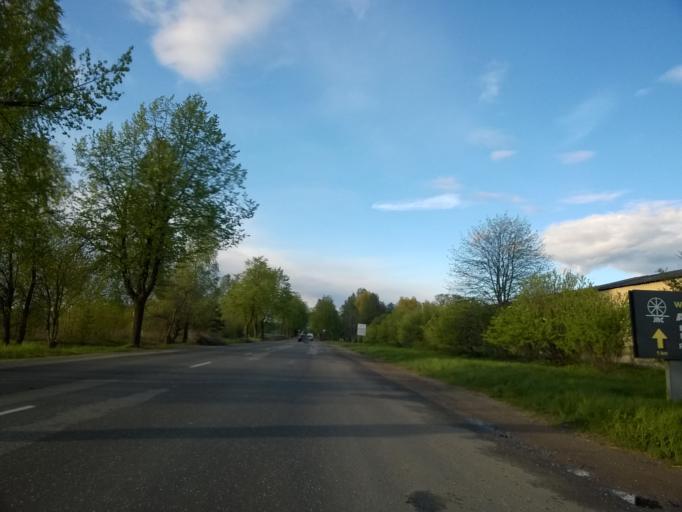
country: LV
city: Tireli
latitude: 56.9397
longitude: 23.6016
